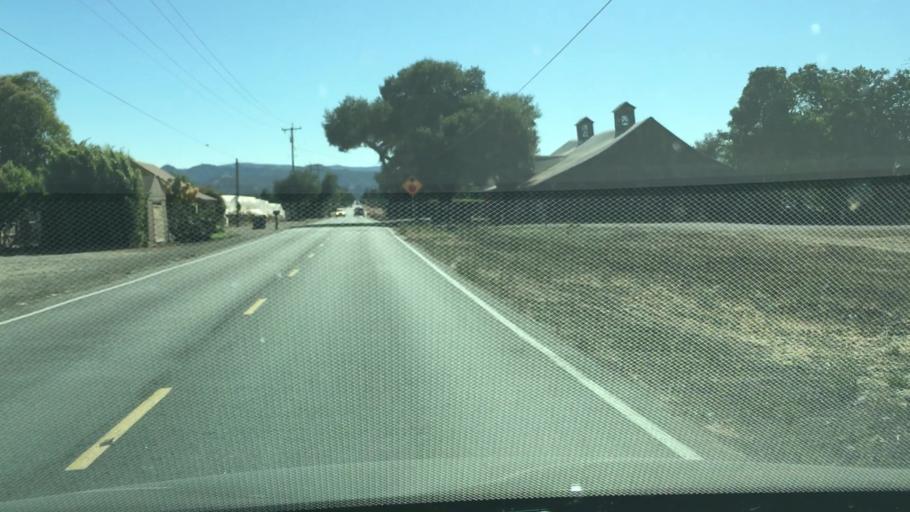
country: US
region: California
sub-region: Santa Clara County
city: San Martin
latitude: 37.1273
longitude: -121.6055
